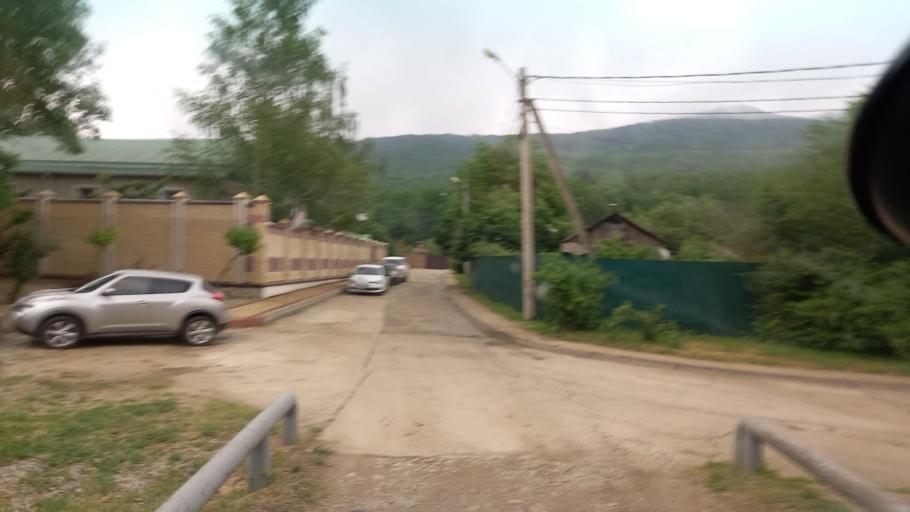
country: RU
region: Krasnodarskiy
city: Azovskaya
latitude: 44.6372
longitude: 38.6167
